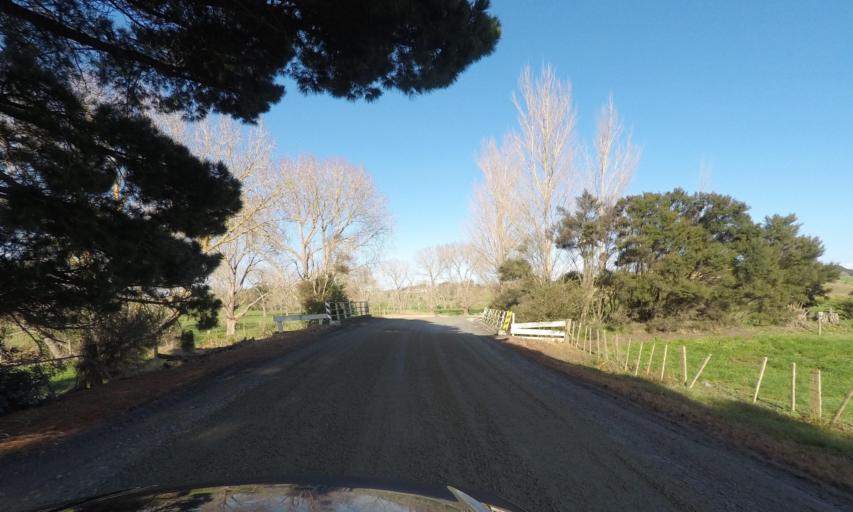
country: NZ
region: Auckland
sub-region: Auckland
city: Wellsford
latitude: -36.1507
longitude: 174.6064
